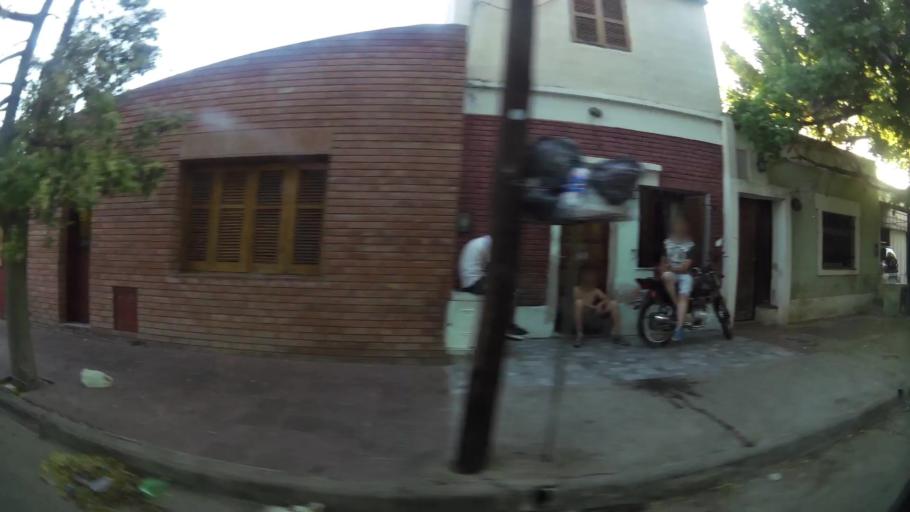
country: AR
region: Cordoba
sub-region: Departamento de Capital
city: Cordoba
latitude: -31.3777
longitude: -64.2098
